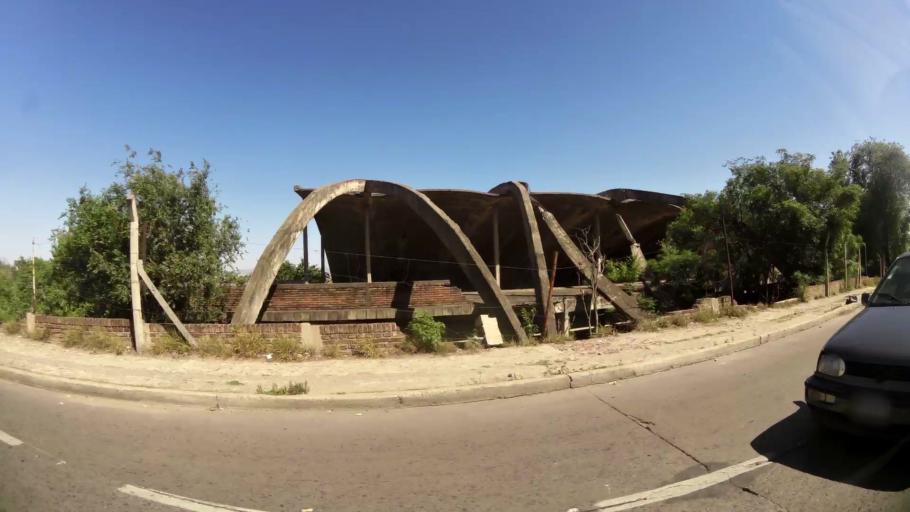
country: AR
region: Cordoba
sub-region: Departamento de Capital
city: Cordoba
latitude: -31.4322
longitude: -64.1399
